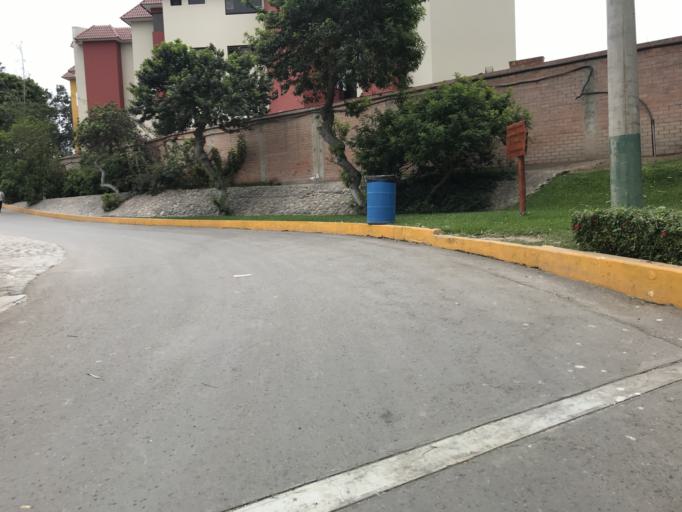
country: PE
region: Callao
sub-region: Callao
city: Callao
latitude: -12.0704
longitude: -77.0880
